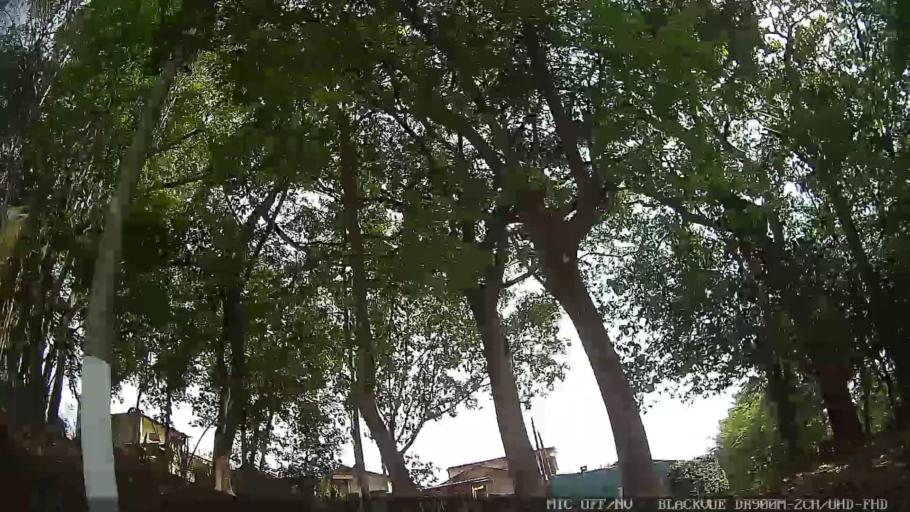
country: BR
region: Sao Paulo
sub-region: Braganca Paulista
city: Braganca Paulista
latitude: -22.9130
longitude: -46.5441
